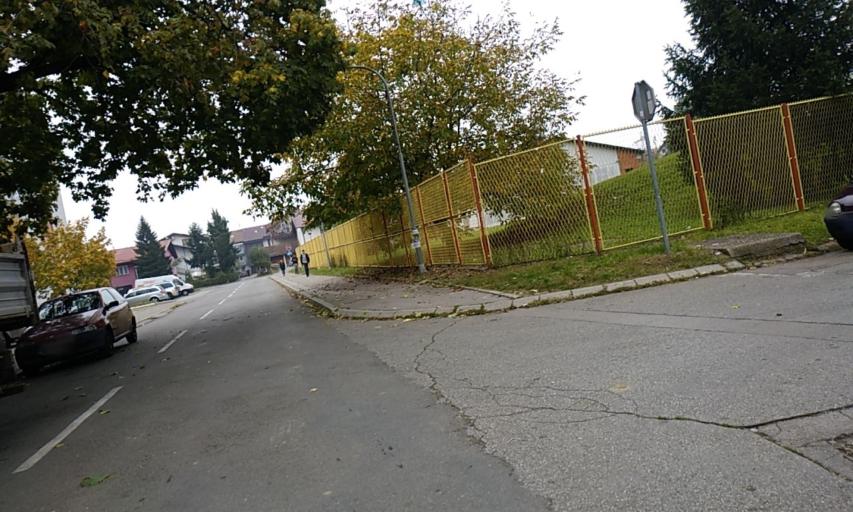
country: BA
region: Republika Srpska
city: Starcevica
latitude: 44.7706
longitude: 17.2069
